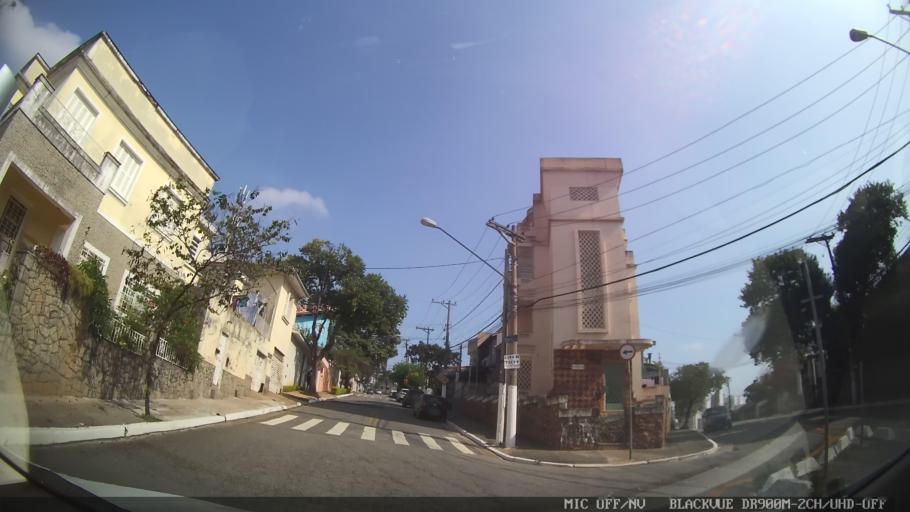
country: BR
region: Sao Paulo
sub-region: Sao Paulo
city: Sao Paulo
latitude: -23.4948
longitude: -46.6194
